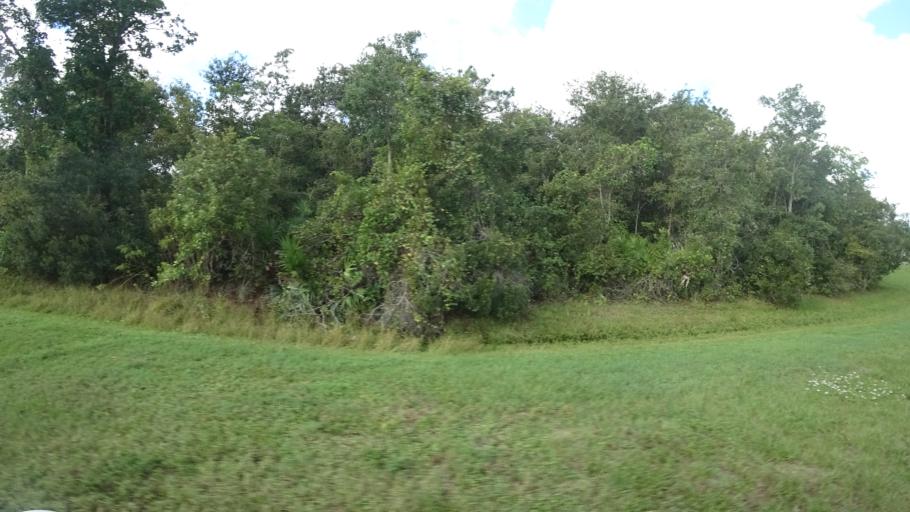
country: US
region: Florida
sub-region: Sarasota County
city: Lake Sarasota
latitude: 27.3626
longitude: -82.2454
